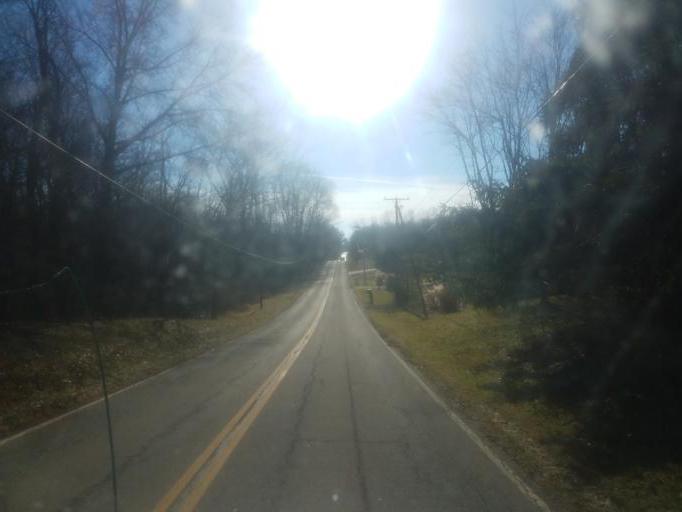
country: US
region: Ohio
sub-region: Richland County
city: Ontario
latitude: 40.7562
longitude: -82.6337
